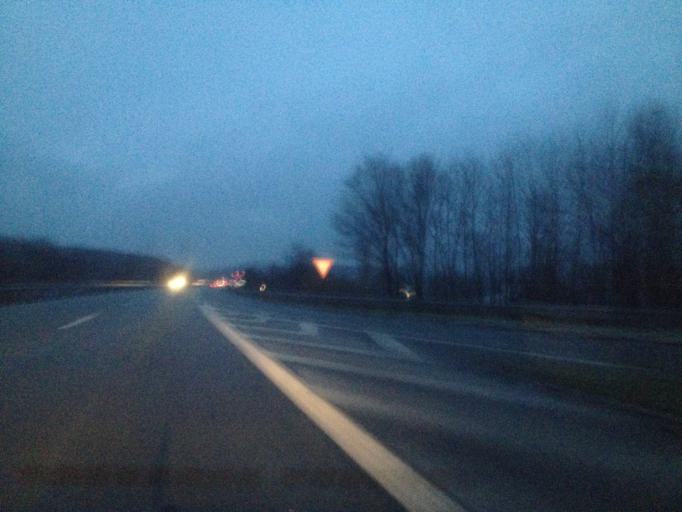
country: DE
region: Rheinland-Pfalz
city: Bad Neuenahr-Ahrweiler
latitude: 50.5727
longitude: 7.1345
